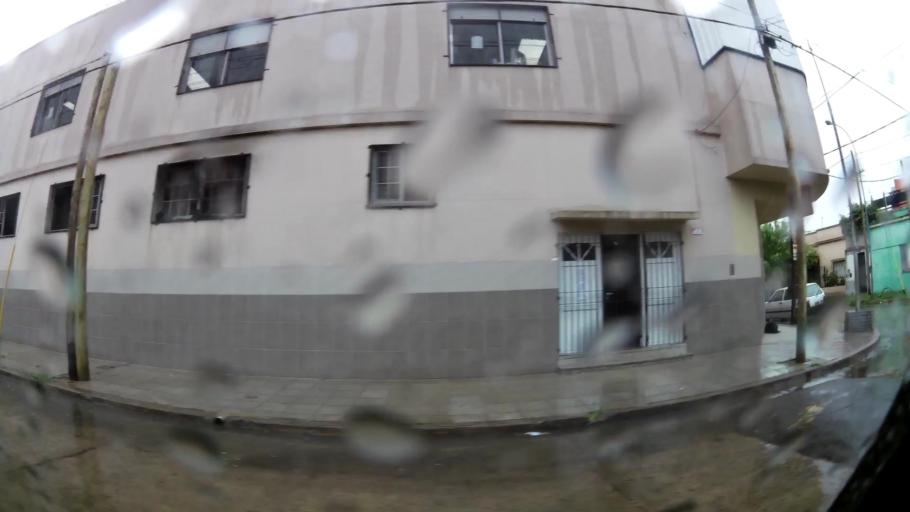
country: AR
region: Buenos Aires
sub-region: Partido de Lanus
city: Lanus
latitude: -34.7174
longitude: -58.4112
